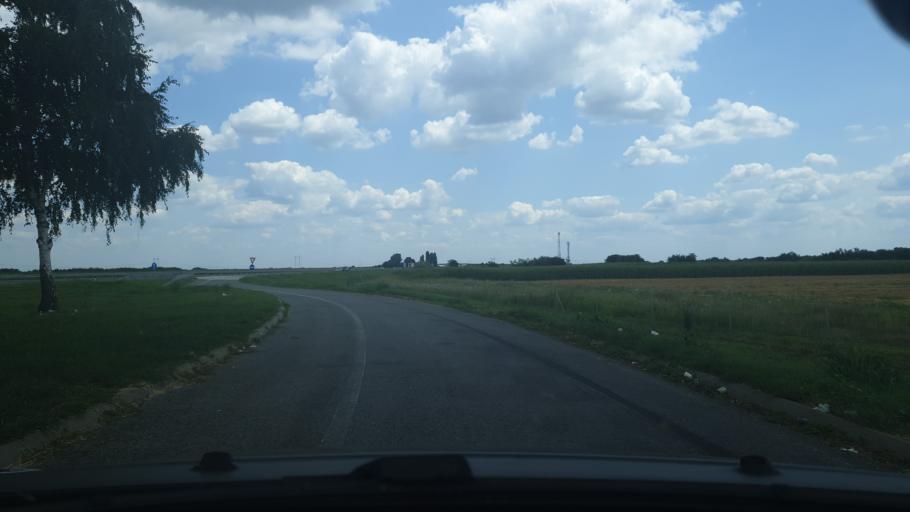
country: RS
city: Sasinci
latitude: 44.9784
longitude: 19.7337
